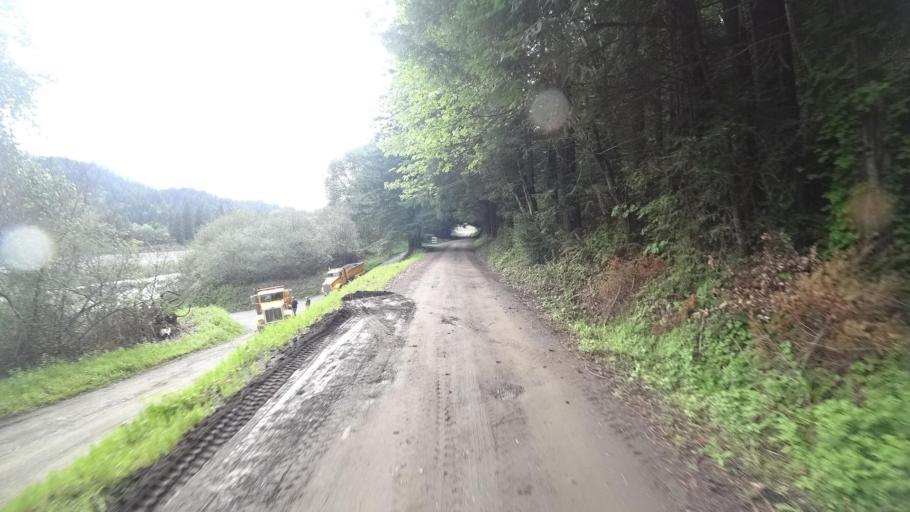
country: US
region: California
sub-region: Humboldt County
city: Redway
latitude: 40.3259
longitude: -123.8397
